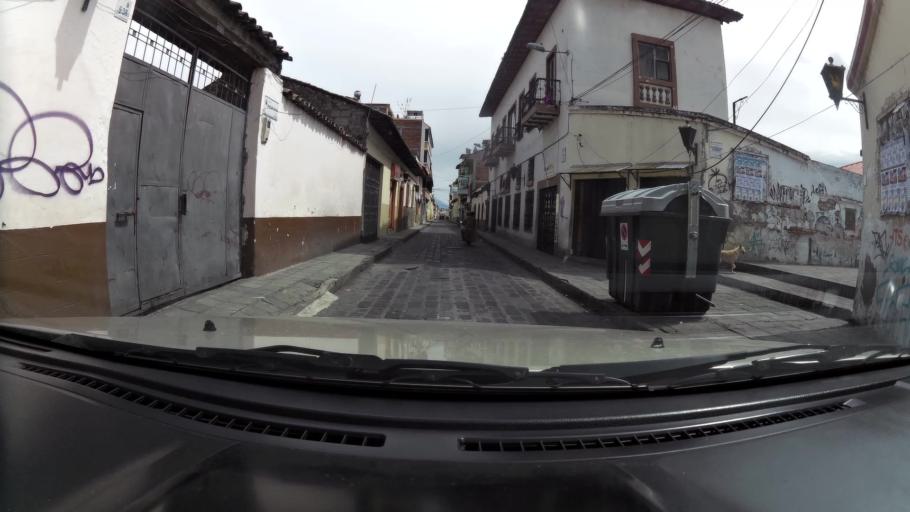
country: EC
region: Cotopaxi
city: Latacunga
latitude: -0.9284
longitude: -78.6108
